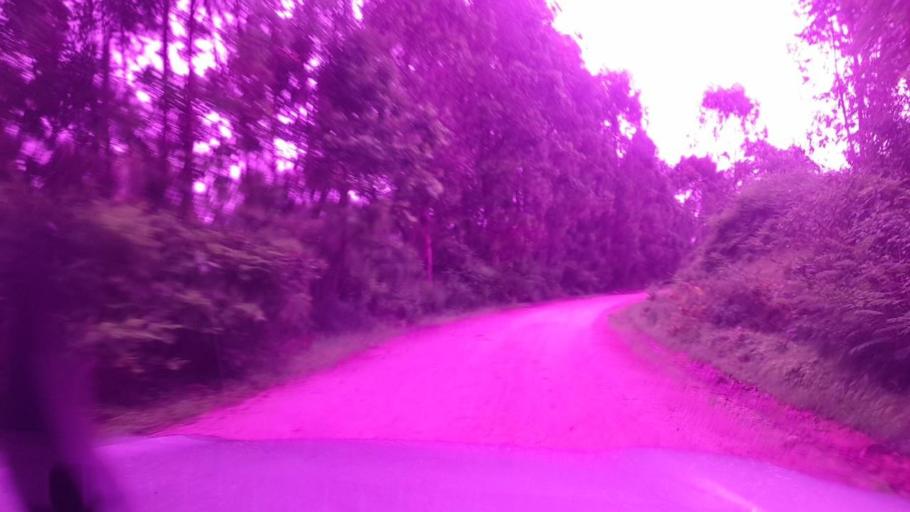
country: ET
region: Southern Nations, Nationalities, and People's Region
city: Bonga
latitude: 7.4579
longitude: 36.1260
